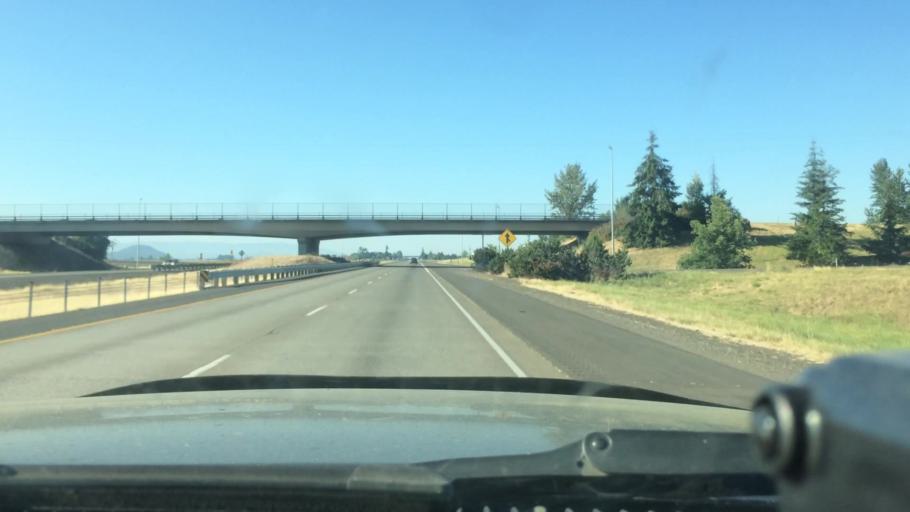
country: US
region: Oregon
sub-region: Linn County
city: Tangent
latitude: 44.5570
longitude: -123.0625
